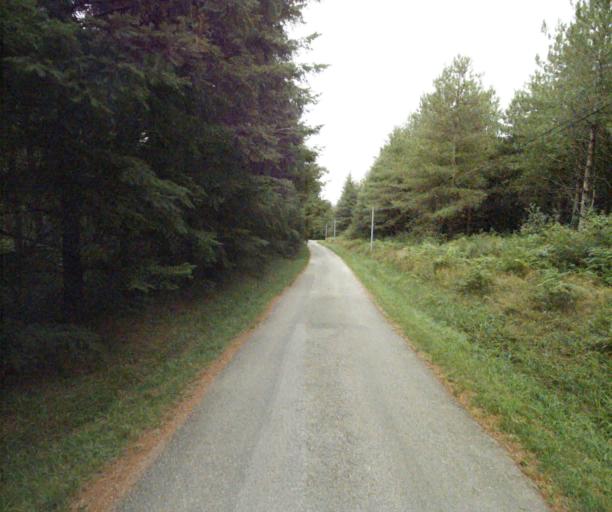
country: FR
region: Midi-Pyrenees
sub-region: Departement du Tarn
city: Soreze
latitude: 43.4178
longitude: 2.0475
